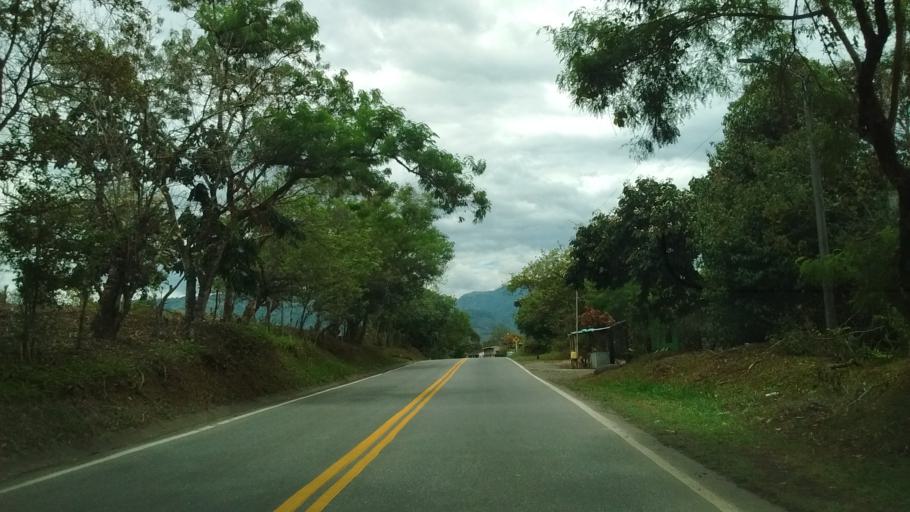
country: CO
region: Cauca
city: La Sierra
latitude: 2.2303
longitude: -76.7901
